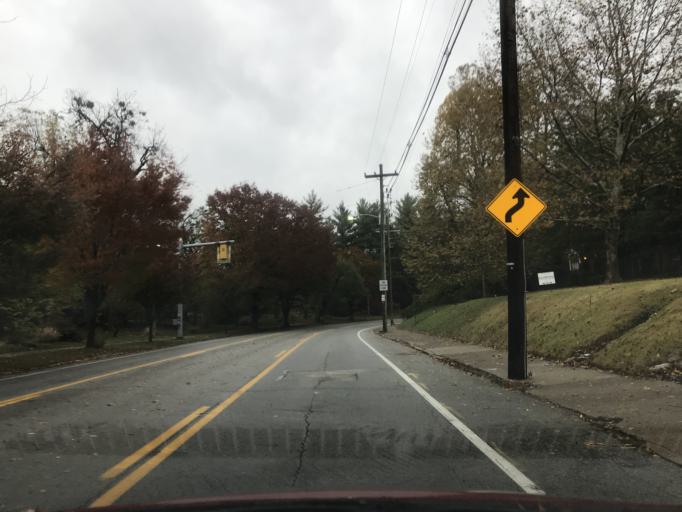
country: US
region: Kentucky
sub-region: Jefferson County
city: Audubon Park
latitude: 38.2430
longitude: -85.7101
